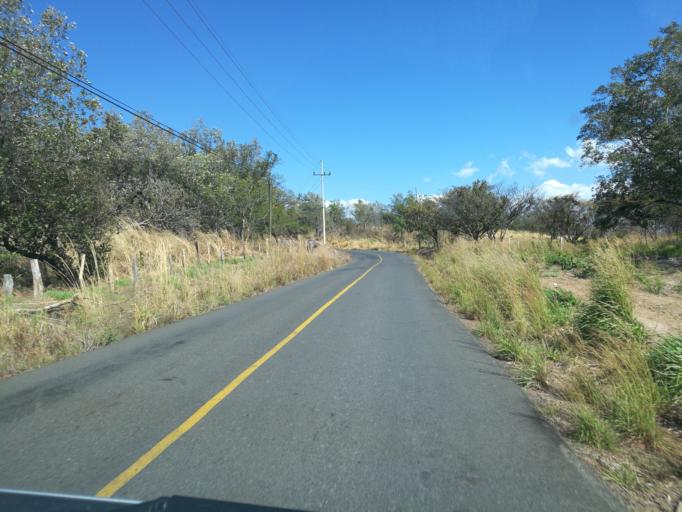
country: CR
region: Guanacaste
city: Liberia
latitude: 10.6672
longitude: -85.4662
